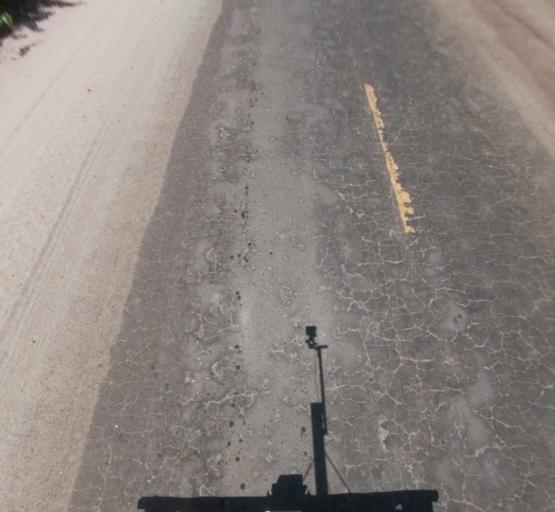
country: US
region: California
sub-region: Fresno County
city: Kerman
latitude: 36.8140
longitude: -120.1509
